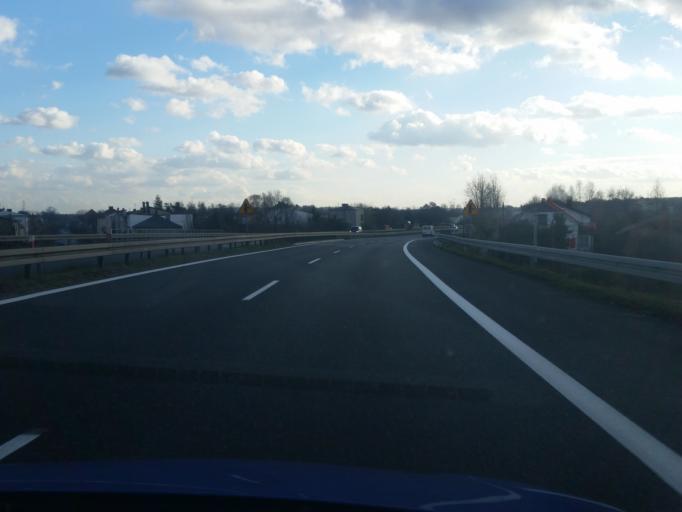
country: PL
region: Silesian Voivodeship
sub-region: Powiat bedzinski
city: Siewierz
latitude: 50.4768
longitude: 19.2280
